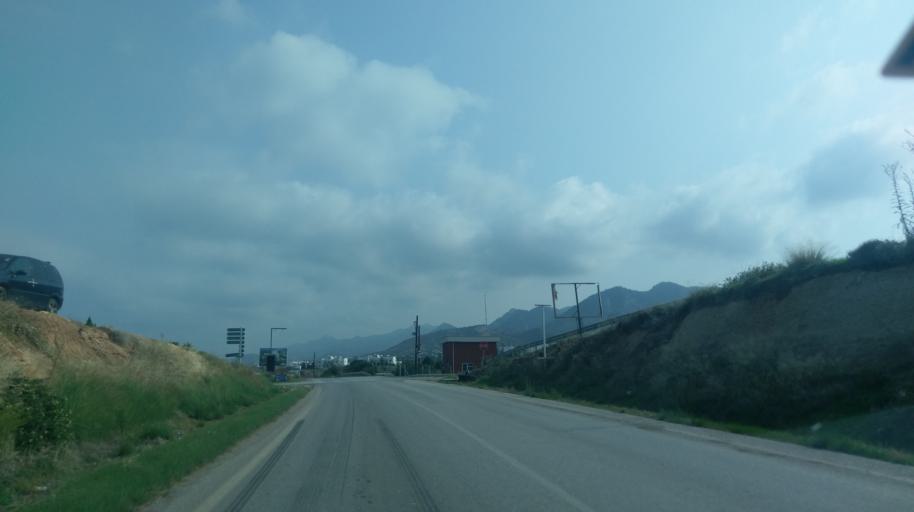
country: CY
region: Ammochostos
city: Lefkonoiko
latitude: 35.3526
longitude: 33.6264
